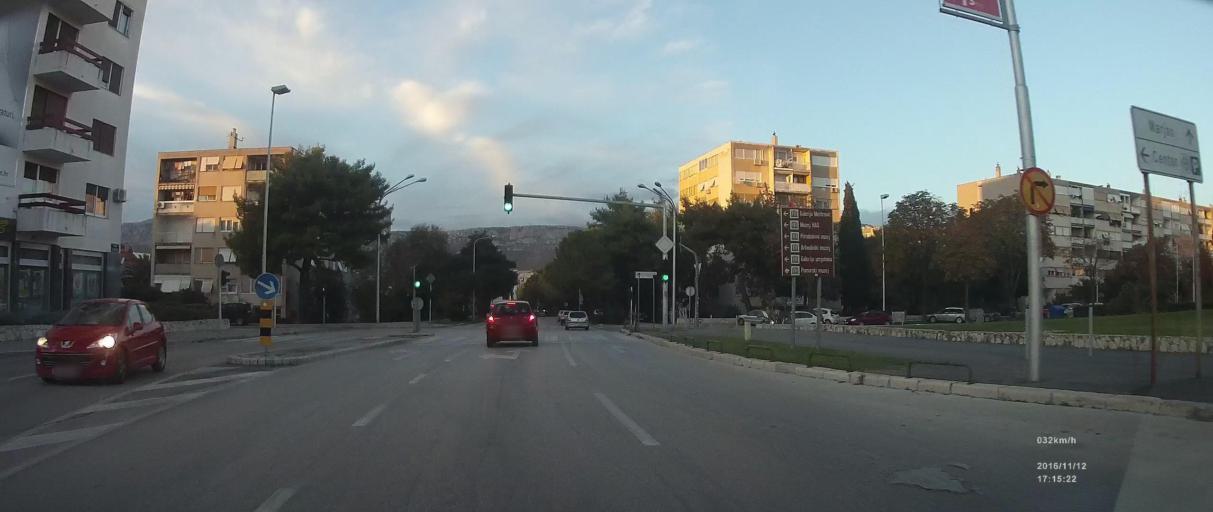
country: HR
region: Splitsko-Dalmatinska
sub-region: Grad Split
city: Split
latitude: 43.5127
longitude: 16.4492
